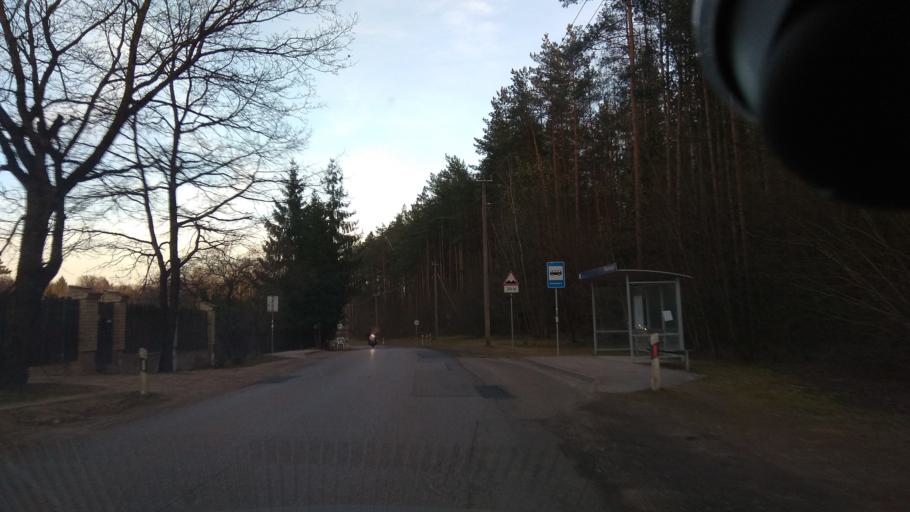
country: LT
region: Vilnius County
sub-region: Vilnius
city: Fabijoniskes
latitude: 54.7547
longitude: 25.2489
